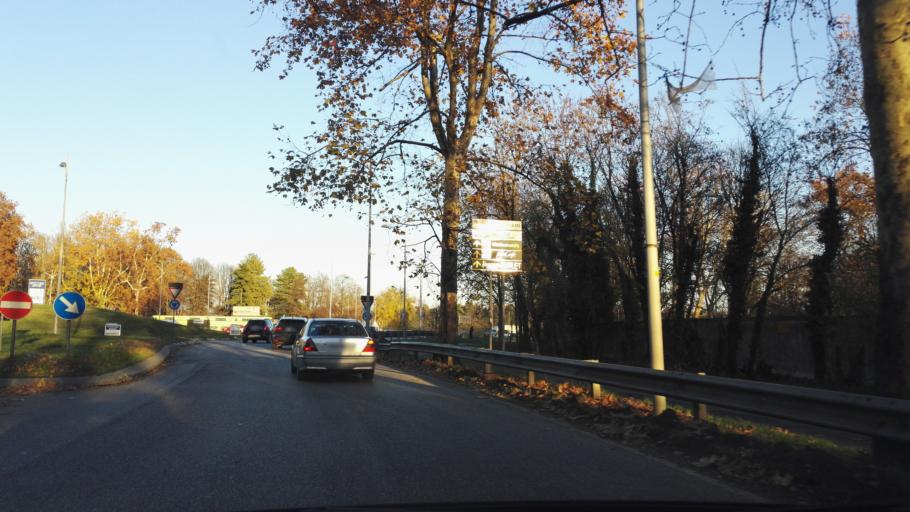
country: IT
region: Lombardy
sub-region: Citta metropolitana di Milano
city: Novegro-Tregarezzo-San Felice
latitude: 45.4652
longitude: 9.2842
